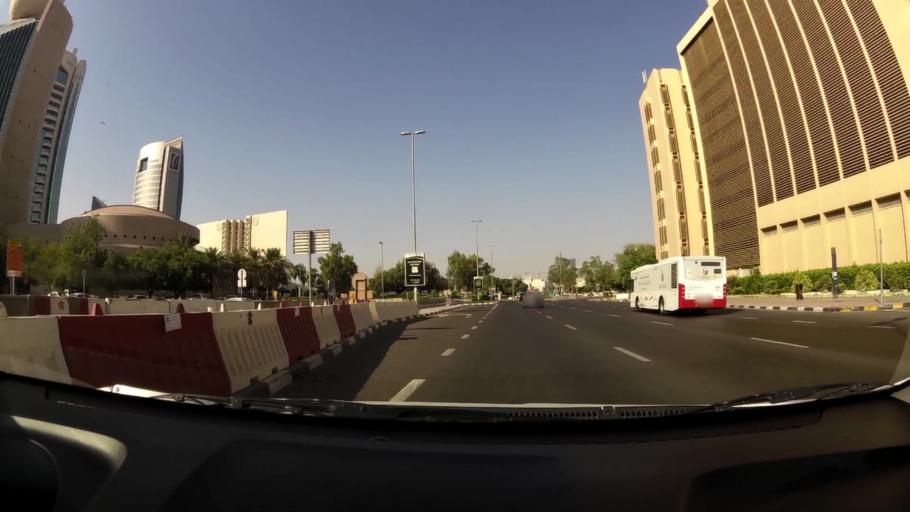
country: AE
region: Ash Shariqah
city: Sharjah
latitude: 25.2637
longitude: 55.3138
